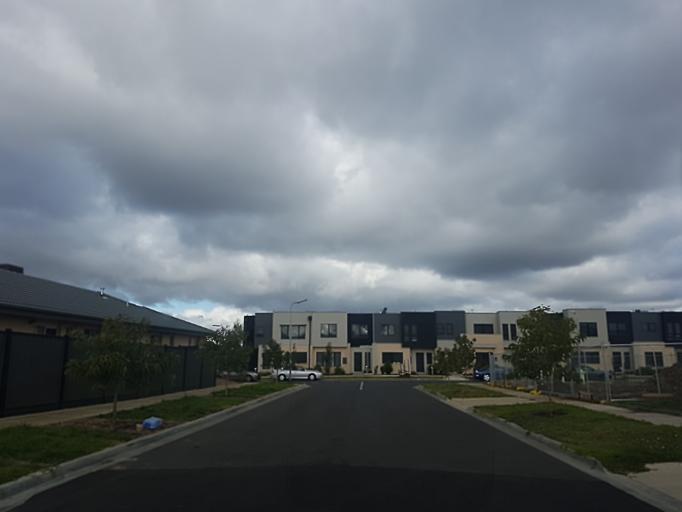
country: AU
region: Victoria
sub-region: Whittlesea
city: Mernda
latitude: -37.5950
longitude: 145.0805
